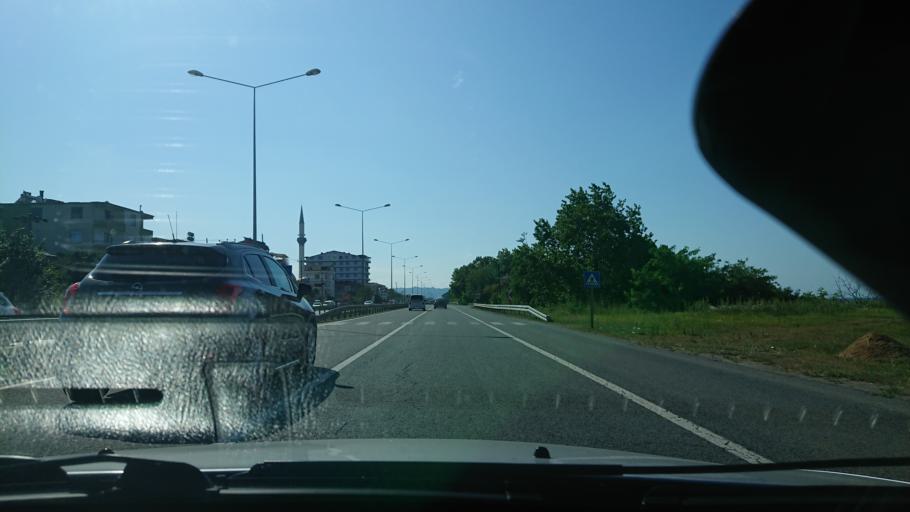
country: TR
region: Ordu
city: Unieh
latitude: 41.1093
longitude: 37.3495
